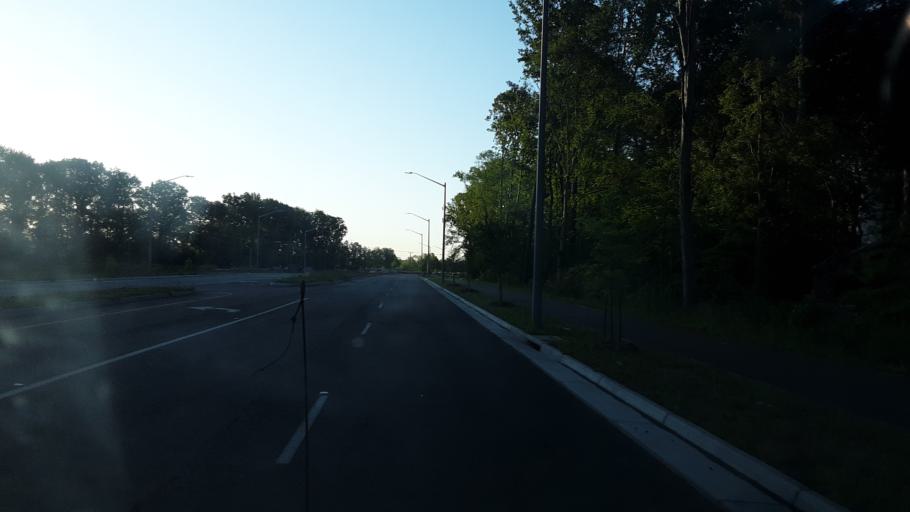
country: US
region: Virginia
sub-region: City of Virginia Beach
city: Virginia Beach
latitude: 36.7588
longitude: -76.0165
